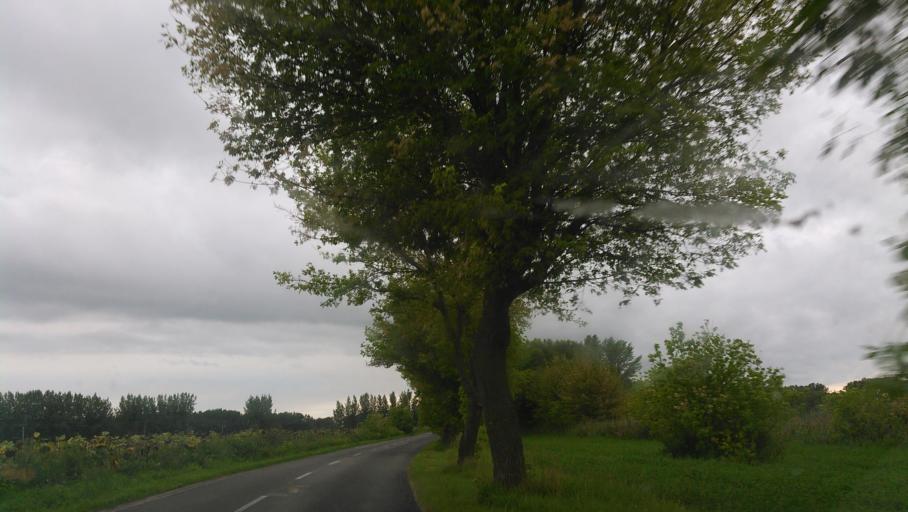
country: SK
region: Trnavsky
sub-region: Okres Dunajska Streda
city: Velky Meder
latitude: 47.9143
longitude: 17.7534
